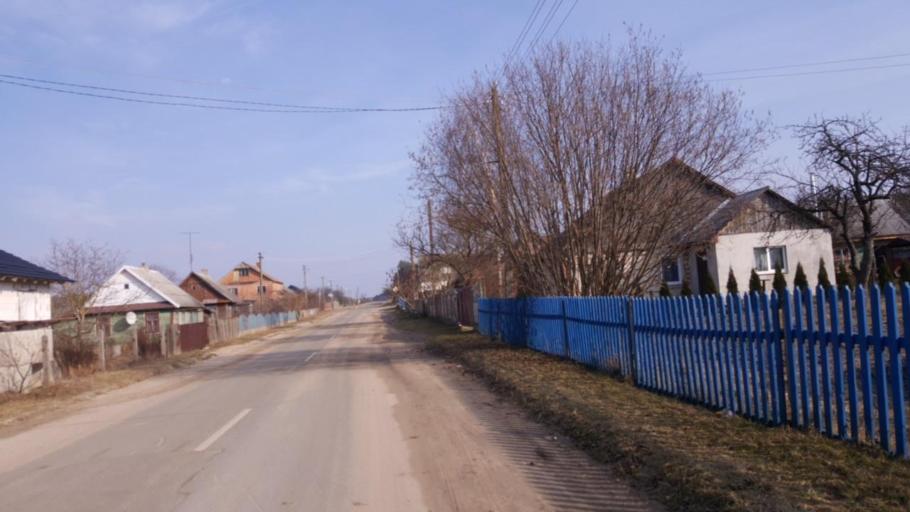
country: BY
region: Brest
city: Kamyanyets
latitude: 52.4072
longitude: 23.8328
